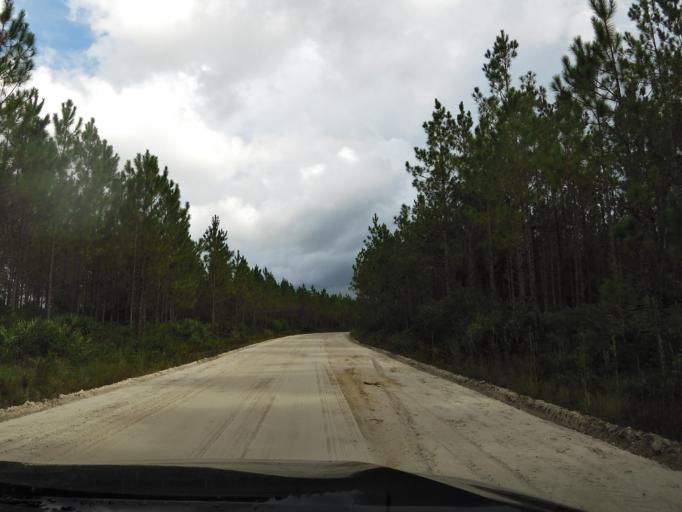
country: US
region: Florida
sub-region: Nassau County
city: Hilliard
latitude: 30.6050
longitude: -82.0693
